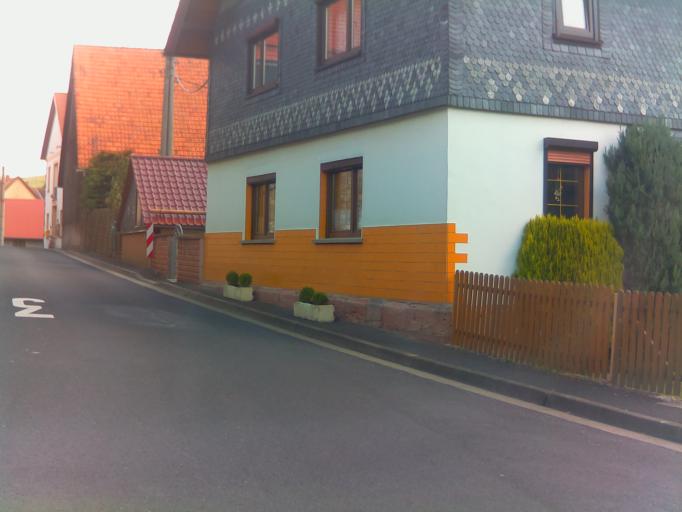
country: DE
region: Thuringia
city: Schmeheim
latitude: 50.5717
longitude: 10.5805
